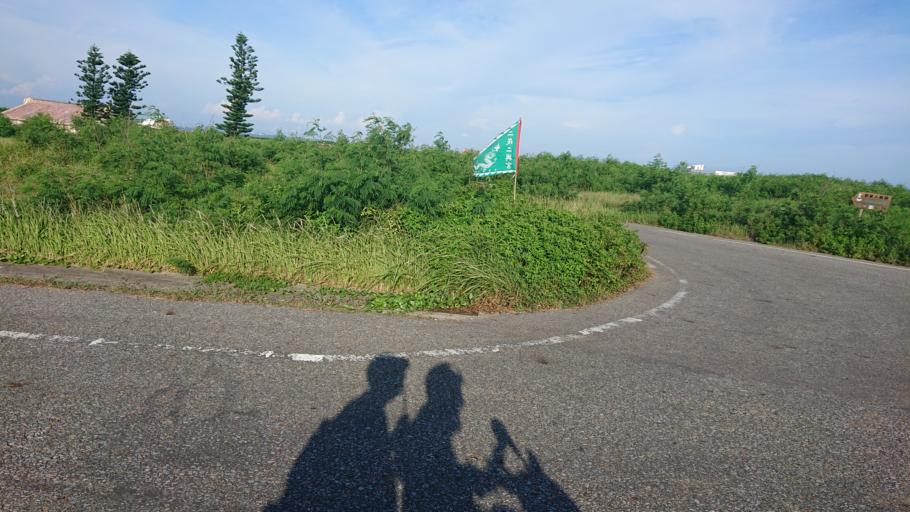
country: TW
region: Taiwan
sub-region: Penghu
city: Ma-kung
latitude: 23.6043
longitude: 119.5169
